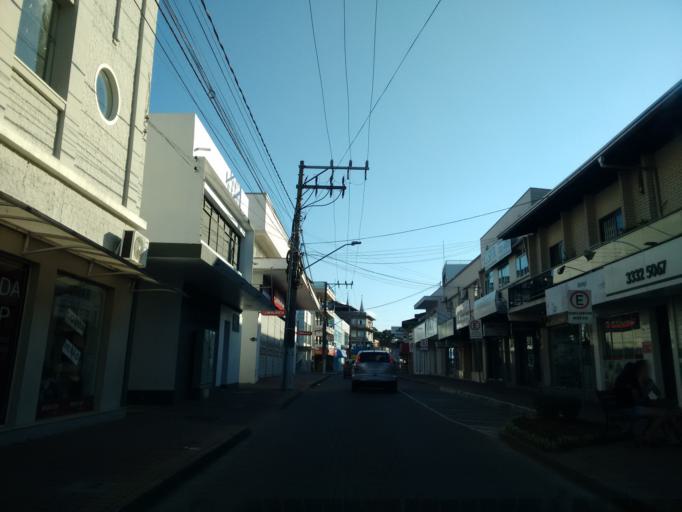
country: BR
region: Santa Catarina
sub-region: Gaspar
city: Gaspar
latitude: -26.9280
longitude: -48.9536
